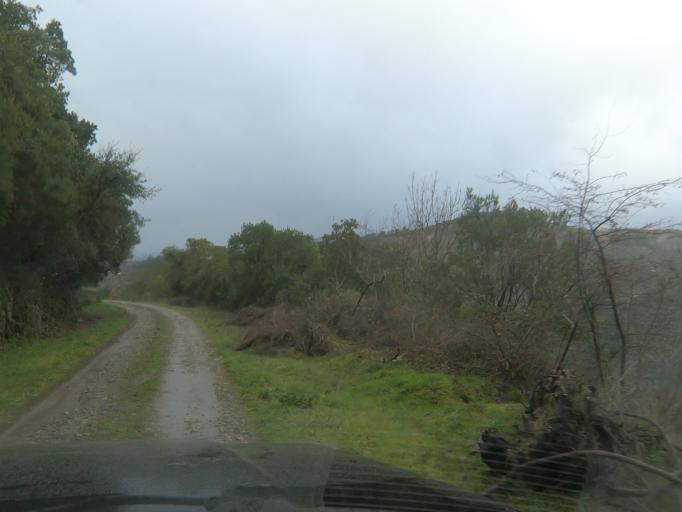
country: PT
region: Vila Real
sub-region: Vila Real
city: Vila Real
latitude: 41.2456
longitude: -7.7469
